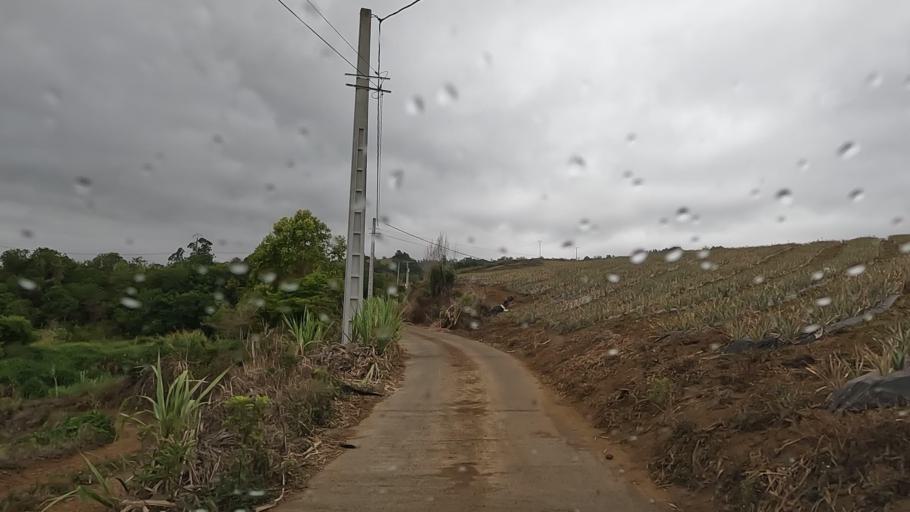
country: RE
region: Reunion
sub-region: Reunion
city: Le Tampon
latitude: -21.2907
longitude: 55.5434
